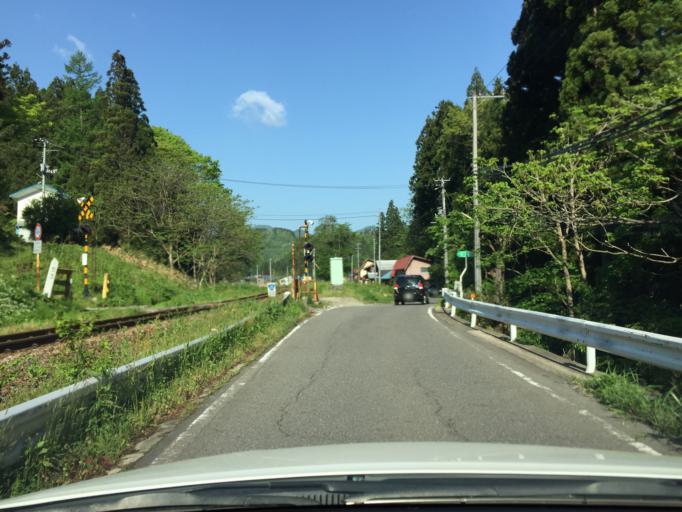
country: JP
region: Fukushima
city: Kitakata
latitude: 37.6674
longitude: 139.6066
